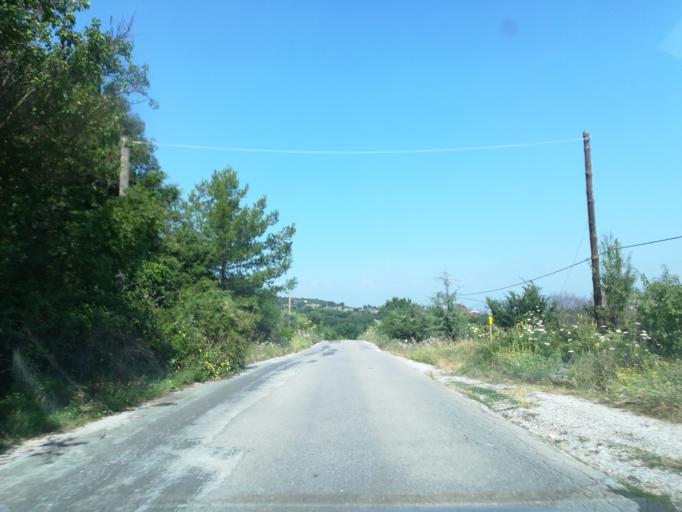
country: GR
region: Central Macedonia
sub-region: Nomos Thessalonikis
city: Asvestochori
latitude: 40.6309
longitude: 23.0307
